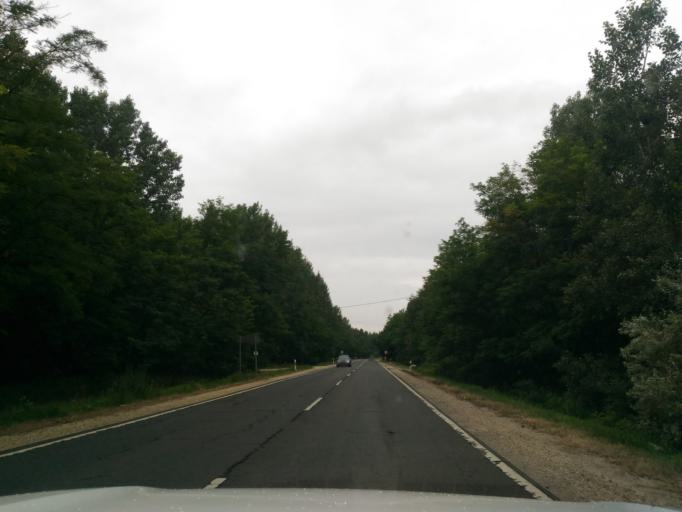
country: HU
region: Pest
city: Alsonemedi
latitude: 47.2935
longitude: 19.1864
